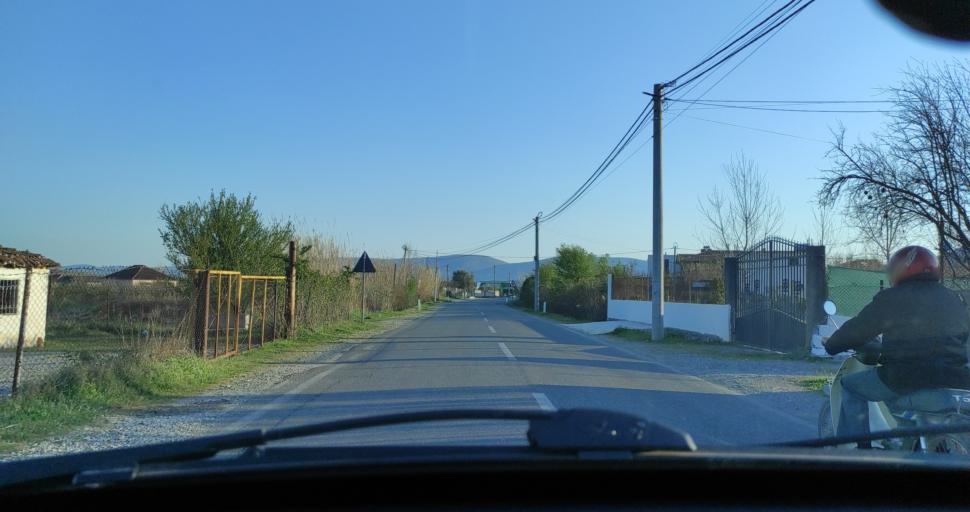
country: AL
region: Shkoder
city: Vukatane
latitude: 41.9691
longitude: 19.5394
